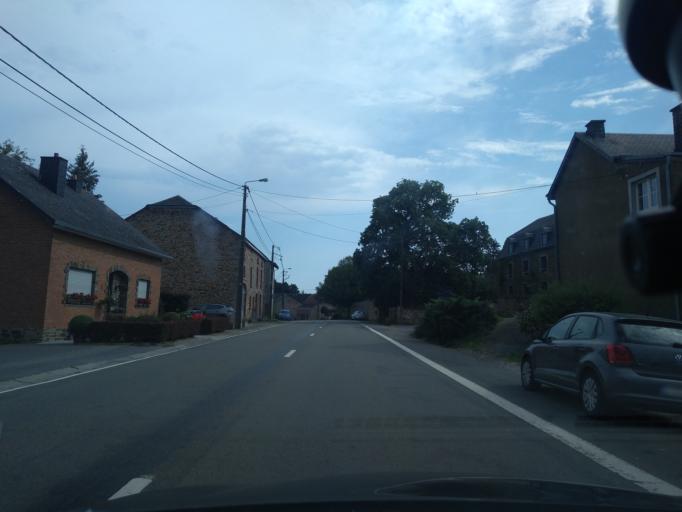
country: BE
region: Wallonia
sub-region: Province du Luxembourg
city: Libin
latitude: 49.9865
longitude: 5.2526
